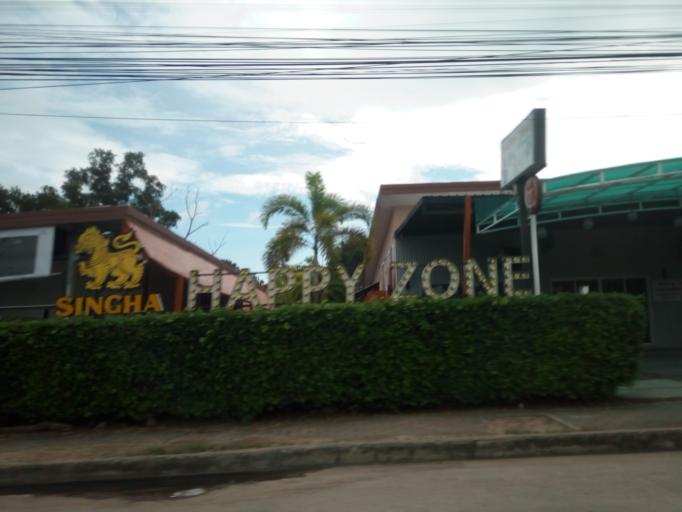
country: TH
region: Phuket
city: Ban Talat Nua
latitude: 7.8802
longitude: 98.3778
